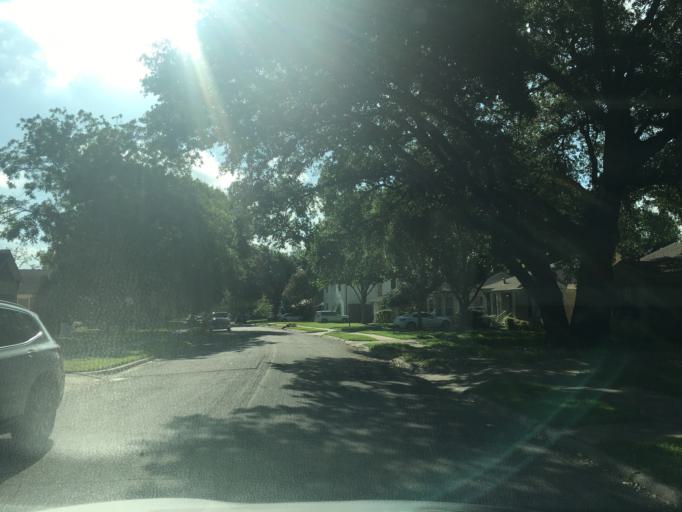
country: US
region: Texas
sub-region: Dallas County
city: Highland Park
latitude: 32.8347
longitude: -96.7579
